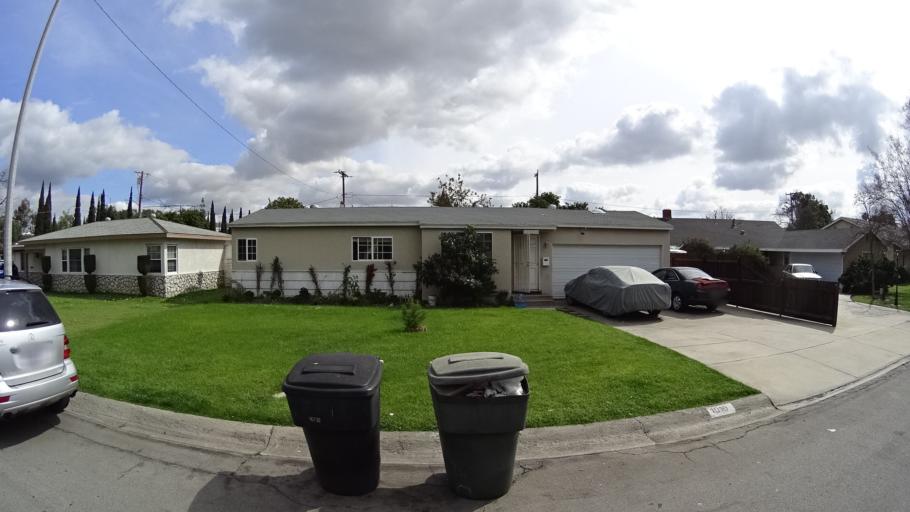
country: US
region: California
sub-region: Orange County
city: Buena Park
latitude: 33.8460
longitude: -117.9652
